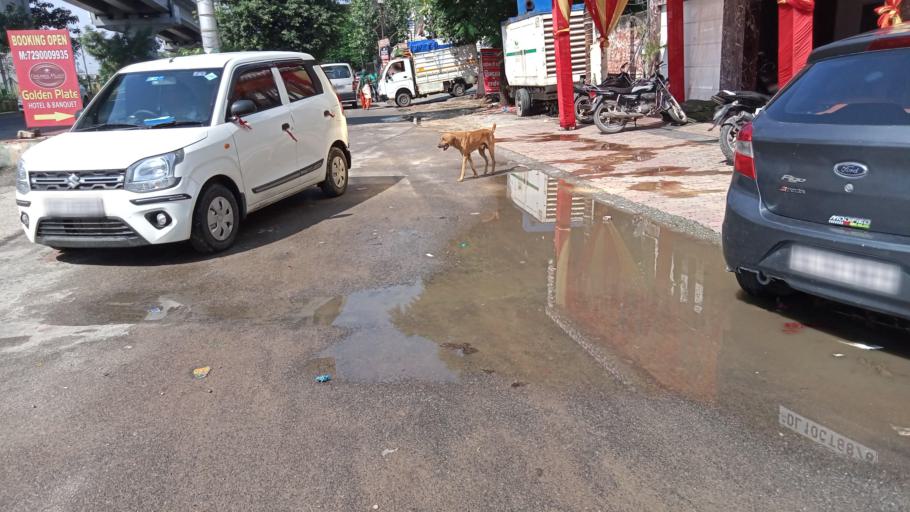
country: IN
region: Uttar Pradesh
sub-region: Ghaziabad
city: Ghaziabad
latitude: 28.6582
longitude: 77.3760
